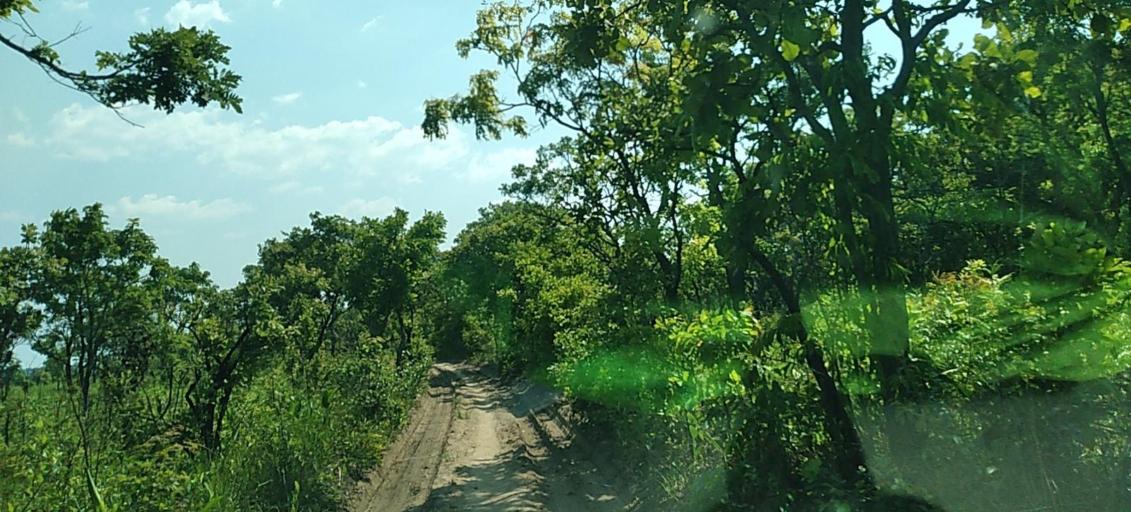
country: CD
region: Katanga
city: Kolwezi
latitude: -11.2587
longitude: 25.0109
